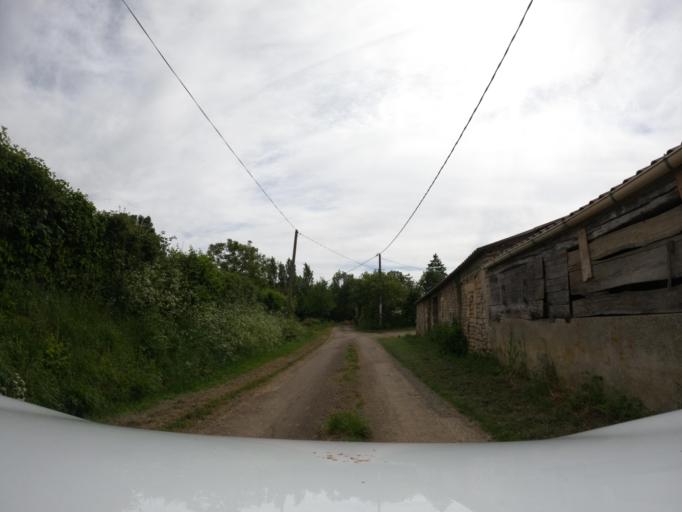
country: FR
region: Pays de la Loire
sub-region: Departement de la Vendee
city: Saint-Hilaire-des-Loges
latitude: 46.4876
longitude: -0.6289
